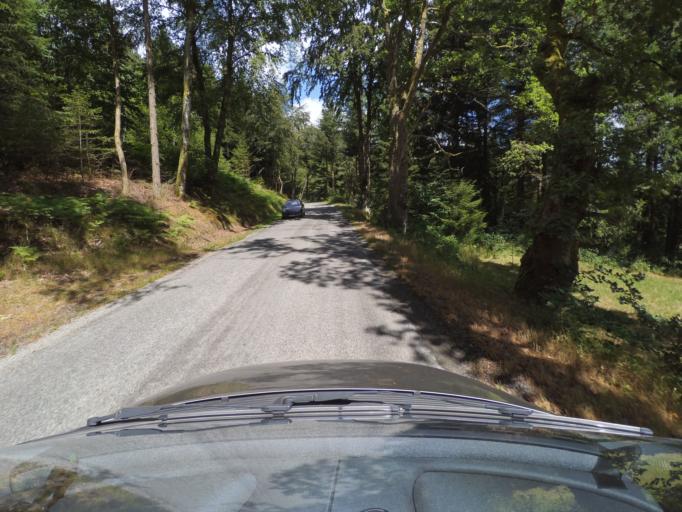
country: FR
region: Limousin
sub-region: Departement de la Creuse
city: Banize
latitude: 45.8038
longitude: 1.9322
